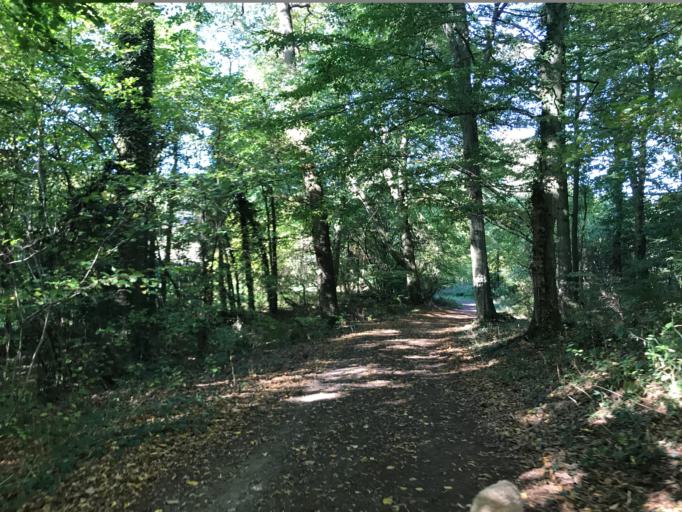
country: DE
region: Rheinland-Pfalz
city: Wolken
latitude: 50.3337
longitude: 7.4439
